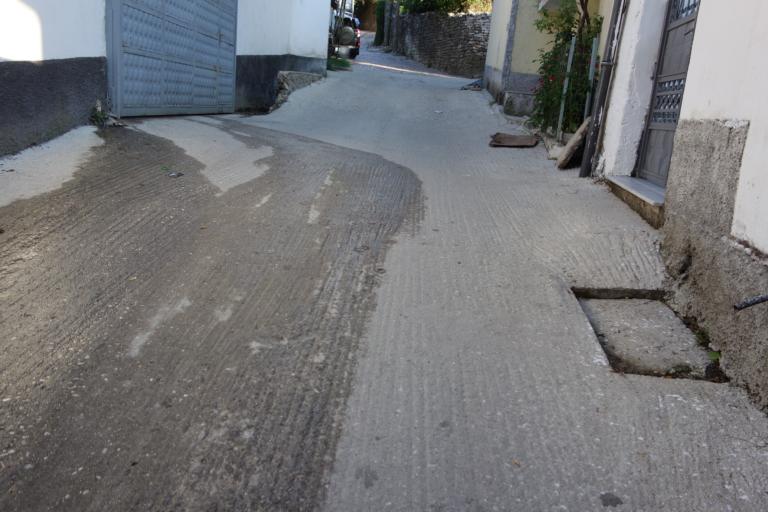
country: AL
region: Gjirokaster
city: Gjirokaster
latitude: 40.0777
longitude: 20.1351
